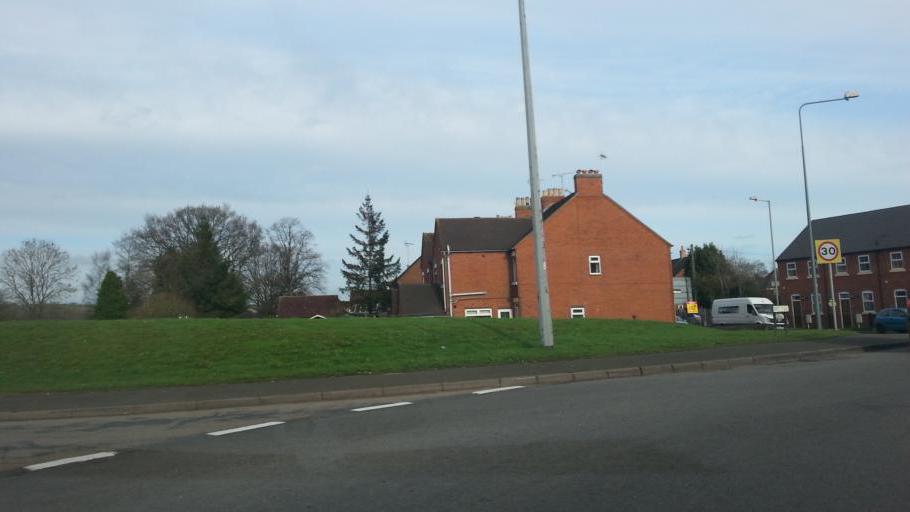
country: GB
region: England
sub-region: Staffordshire
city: Uttoxeter
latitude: 52.9021
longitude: -1.8603
